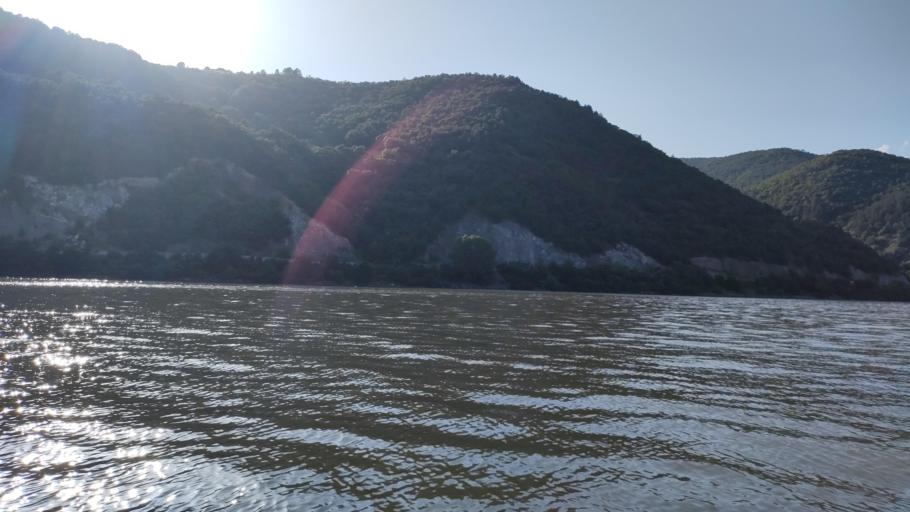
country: RO
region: Mehedinti
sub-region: Comuna Svinita
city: Svinita
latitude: 44.4962
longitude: 22.1892
